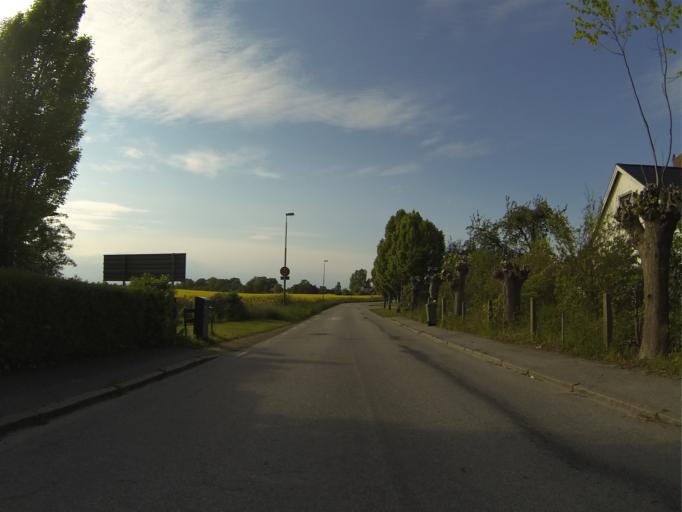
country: SE
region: Skane
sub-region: Svedala Kommun
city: Klagerup
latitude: 55.6469
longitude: 13.2670
